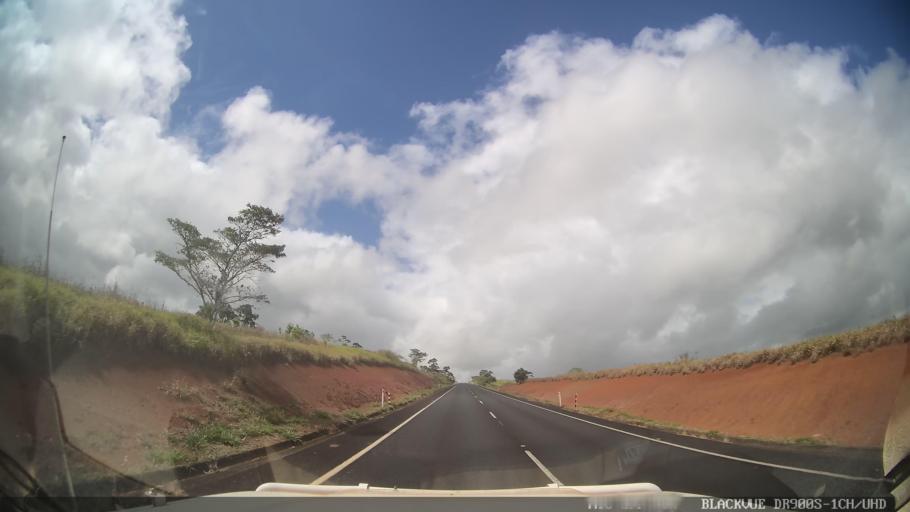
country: AU
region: Queensland
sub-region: Tablelands
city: Atherton
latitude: -17.2945
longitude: 145.6177
